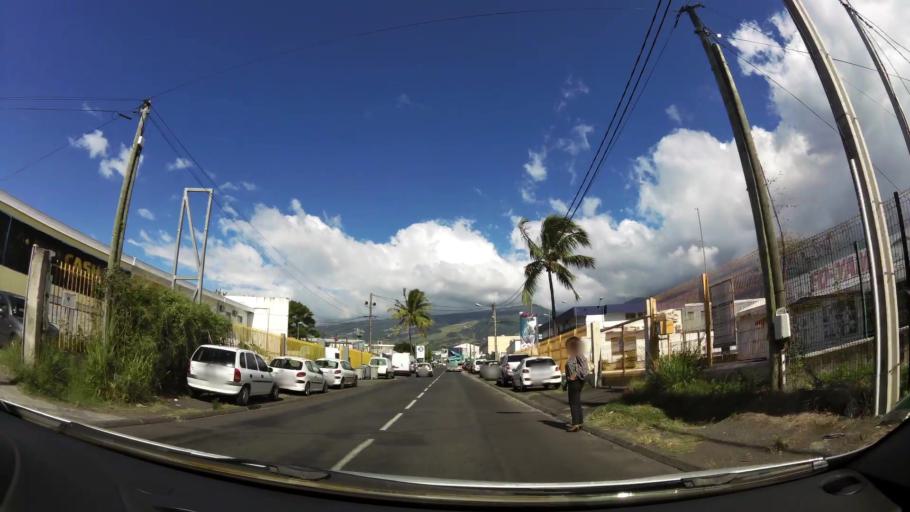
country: RE
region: Reunion
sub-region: Reunion
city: Saint-Denis
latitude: -20.8934
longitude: 55.4959
